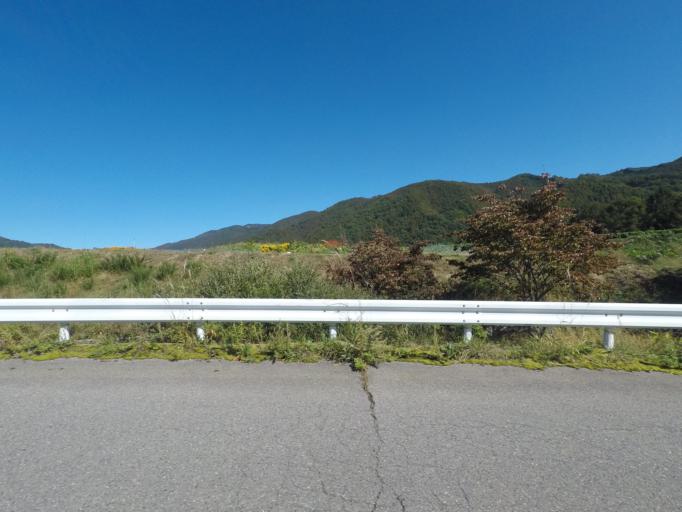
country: JP
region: Nagano
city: Tatsuno
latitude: 35.9756
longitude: 137.7445
